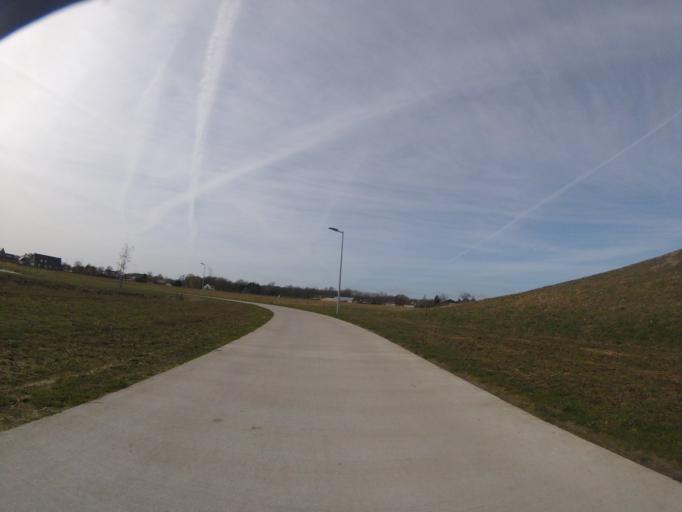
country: NL
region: North Holland
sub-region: Gemeente Bloemendaal
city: Bennebroek
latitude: 52.3191
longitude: 4.6187
